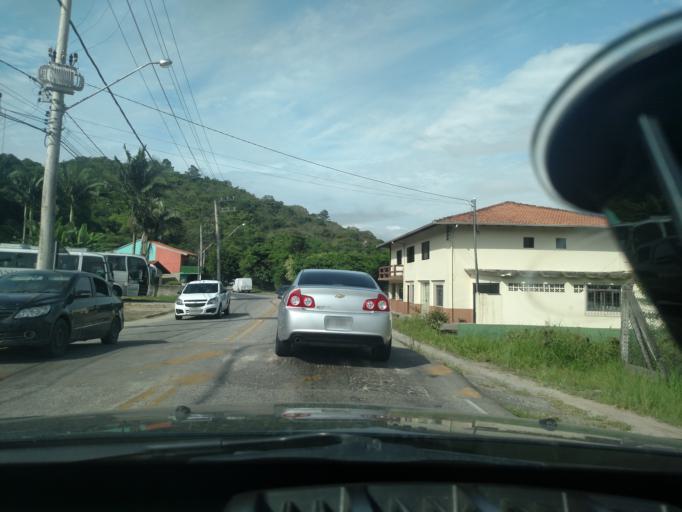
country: BR
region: Santa Catarina
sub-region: Porto Belo
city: Porto Belo
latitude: -27.1458
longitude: -48.5320
